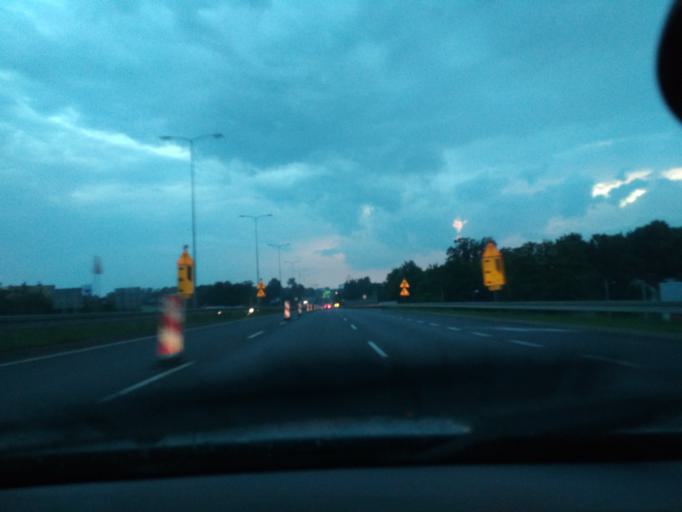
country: PL
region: Silesian Voivodeship
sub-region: Zabrze
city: Zabrze
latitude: 50.2929
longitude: 18.7989
